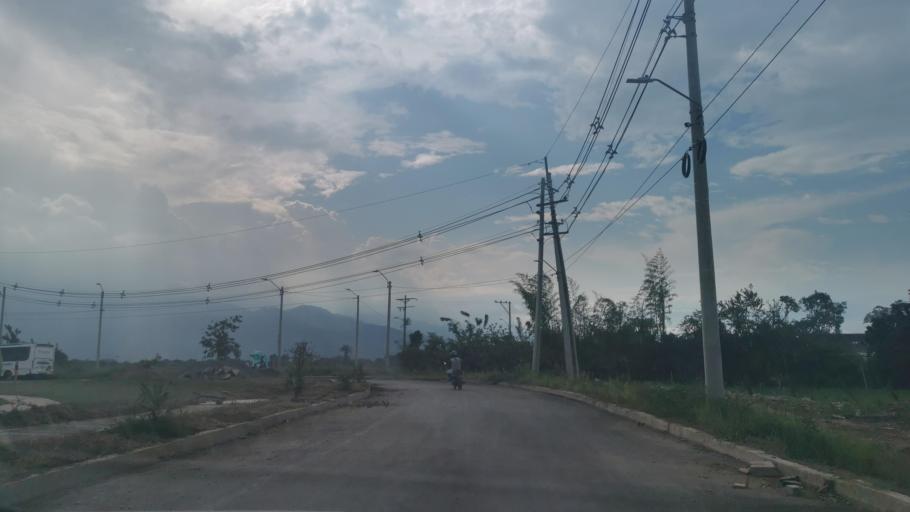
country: CO
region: Valle del Cauca
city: Jamundi
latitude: 3.2371
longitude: -76.5250
